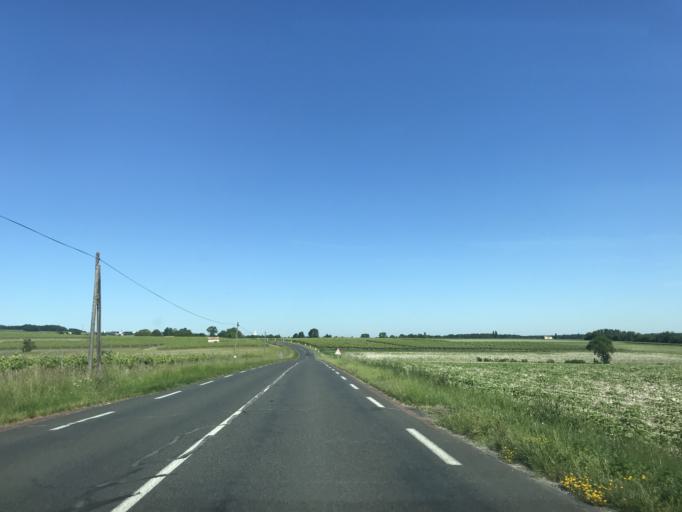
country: FR
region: Poitou-Charentes
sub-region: Departement de la Charente
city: Barbezieux-Saint-Hilaire
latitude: 45.5045
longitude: -0.2578
